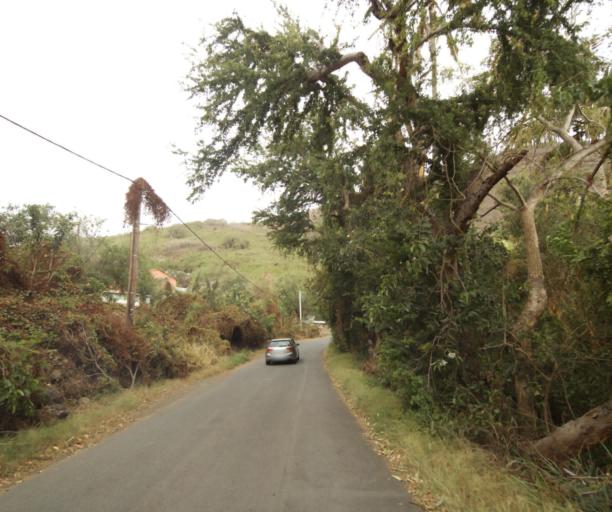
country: RE
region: Reunion
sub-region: Reunion
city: Saint-Paul
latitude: -21.0039
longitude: 55.3000
